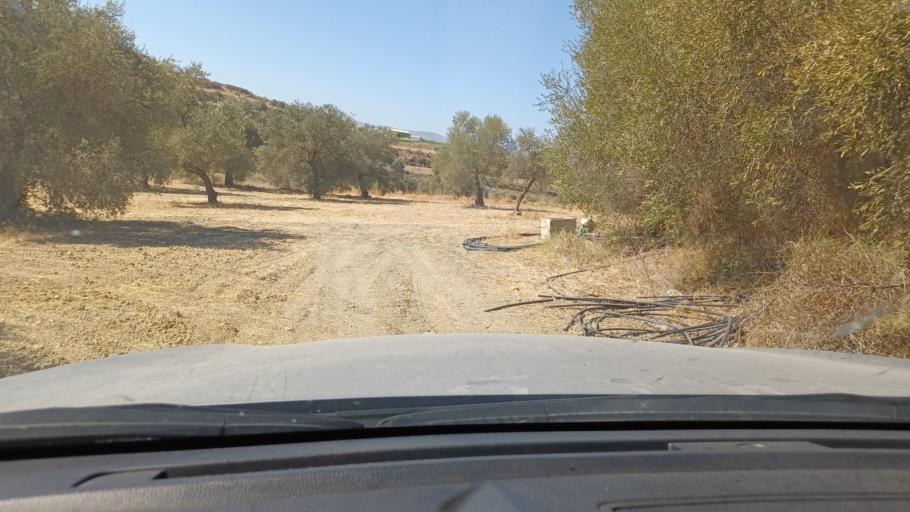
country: CY
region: Pafos
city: Polis
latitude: 35.0272
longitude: 32.4586
